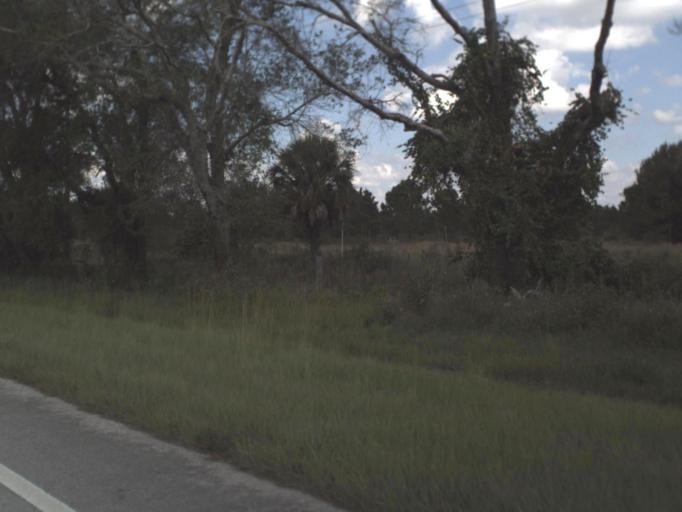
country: US
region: Florida
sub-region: Okeechobee County
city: Okeechobee
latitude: 27.3646
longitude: -81.0633
